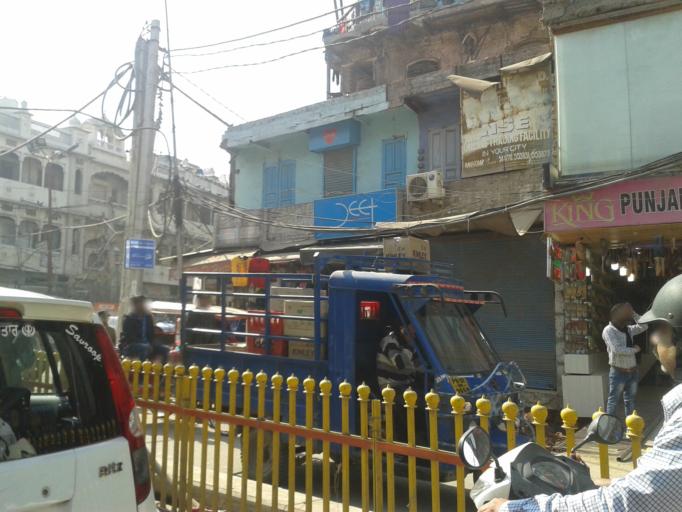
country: IN
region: Punjab
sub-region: Amritsar
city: Amritsar
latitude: 31.6228
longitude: 74.8796
